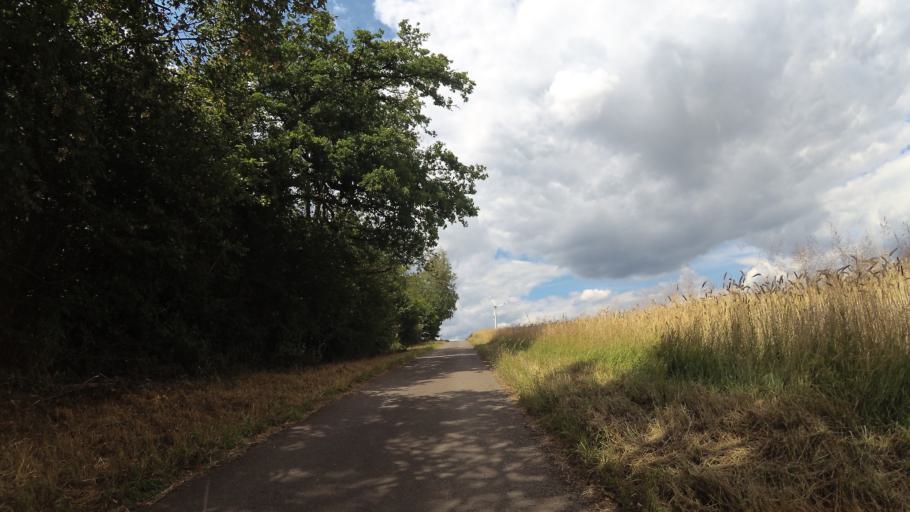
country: DE
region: Rheinland-Pfalz
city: Breitenbach
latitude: 49.4654
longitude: 7.2438
